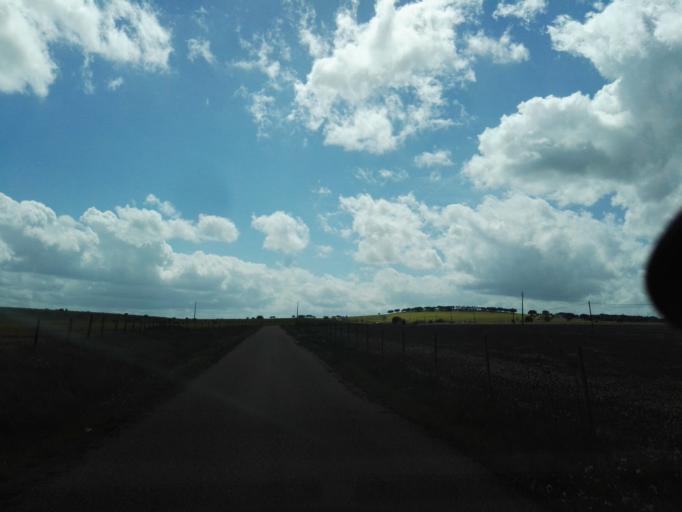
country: PT
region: Portalegre
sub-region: Elvas
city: Elvas
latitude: 38.9636
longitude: -7.1746
